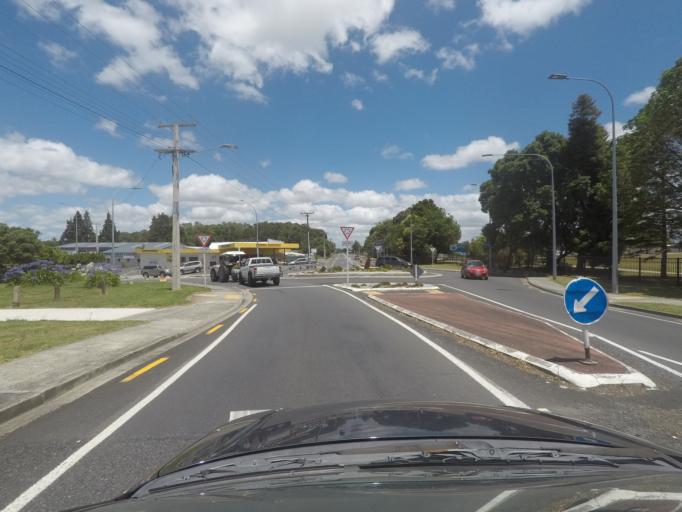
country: NZ
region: Northland
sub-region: Whangarei
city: Whangarei
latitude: -35.7568
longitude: 174.3682
